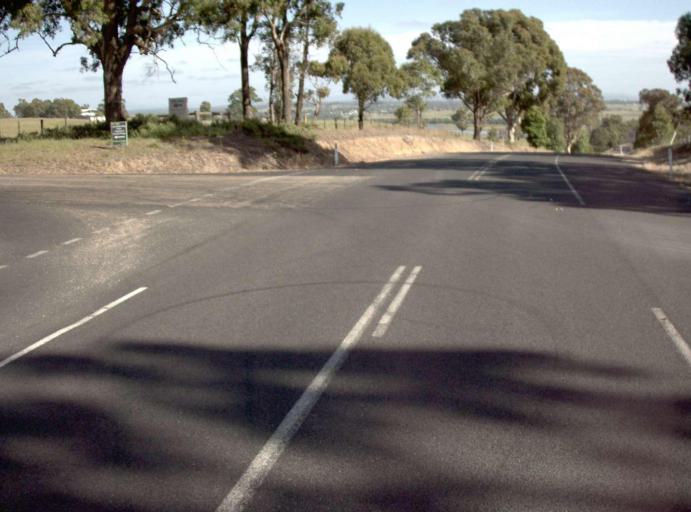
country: AU
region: Victoria
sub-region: East Gippsland
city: Lakes Entrance
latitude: -37.8580
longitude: 147.8454
